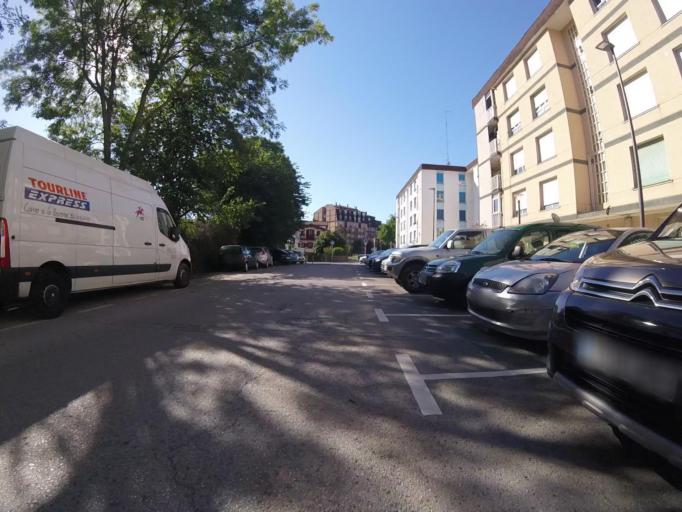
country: ES
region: Basque Country
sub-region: Provincia de Guipuzcoa
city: Irun
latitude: 43.3362
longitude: -1.7805
